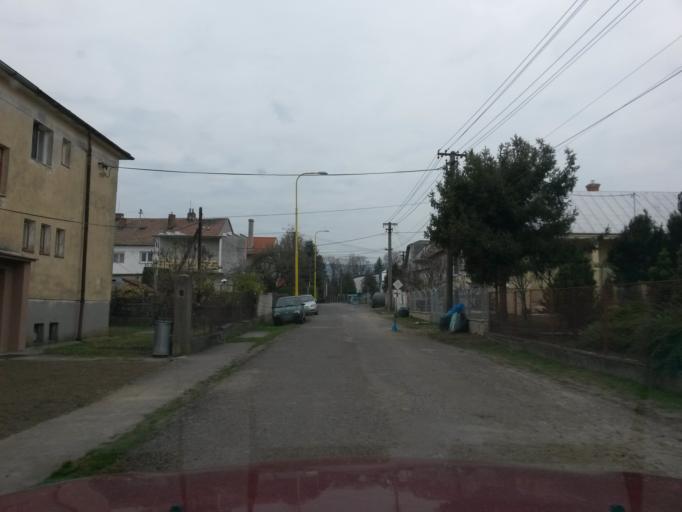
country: SK
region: Kosicky
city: Secovce
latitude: 48.7055
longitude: 21.6509
